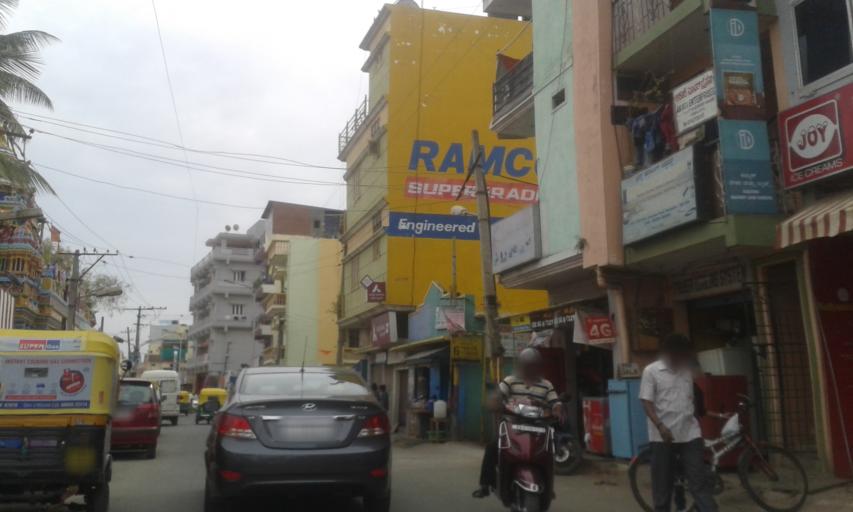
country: IN
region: Karnataka
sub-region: Bangalore Urban
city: Bangalore
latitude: 12.9518
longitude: 77.6097
